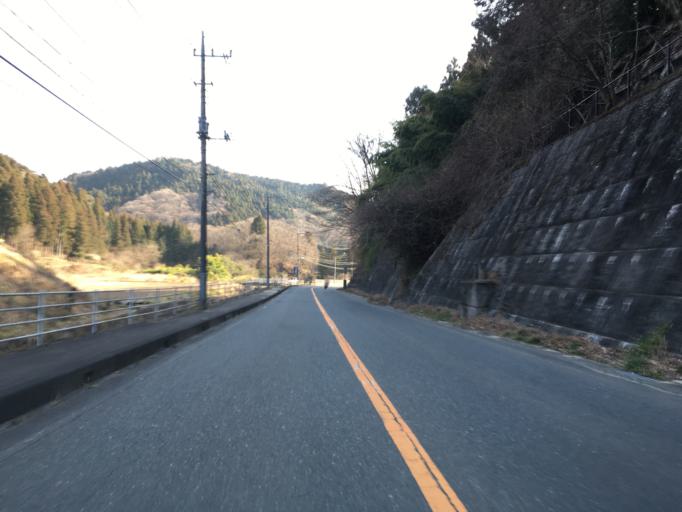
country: JP
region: Ibaraki
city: Daigo
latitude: 36.7243
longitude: 140.5084
